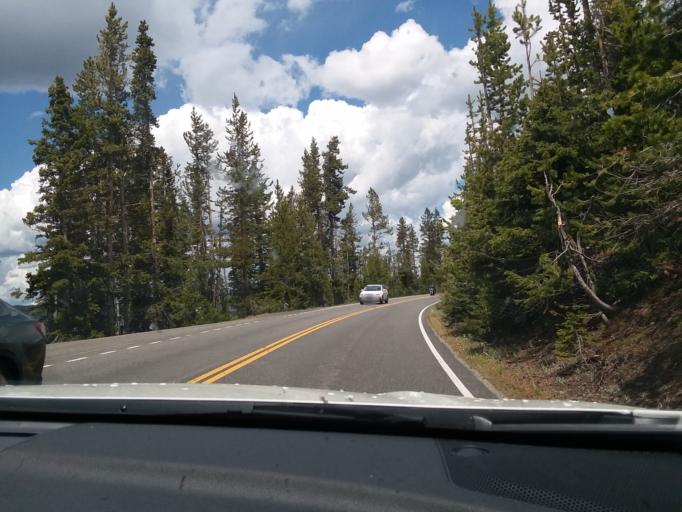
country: US
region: Montana
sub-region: Gallatin County
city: West Yellowstone
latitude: 44.2853
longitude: -110.6273
